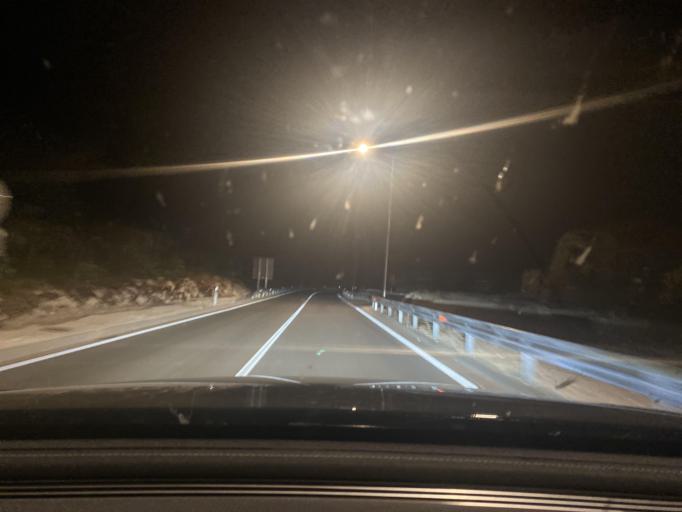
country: BA
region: Federation of Bosnia and Herzegovina
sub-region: Hercegovacko-Bosanski Kanton
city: Neum
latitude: 42.8639
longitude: 17.5643
